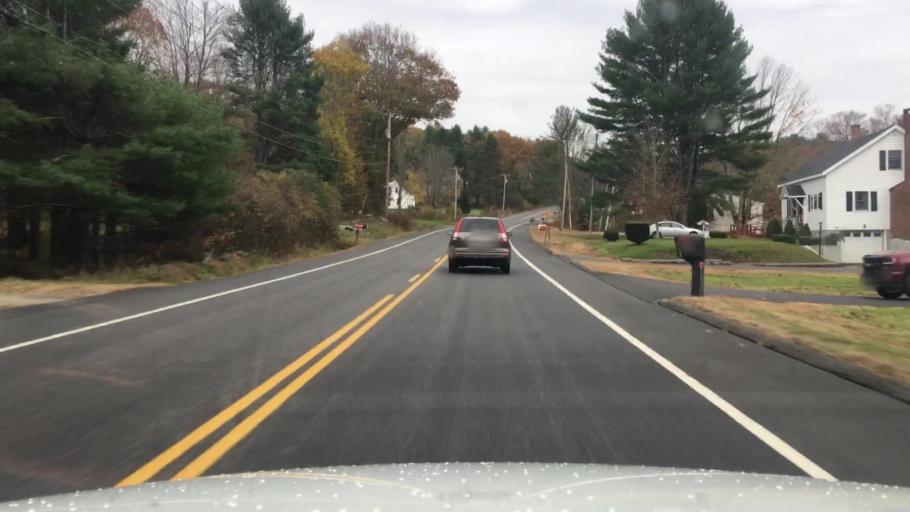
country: US
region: Maine
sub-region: Kennebec County
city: Pittston
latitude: 44.1866
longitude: -69.7459
